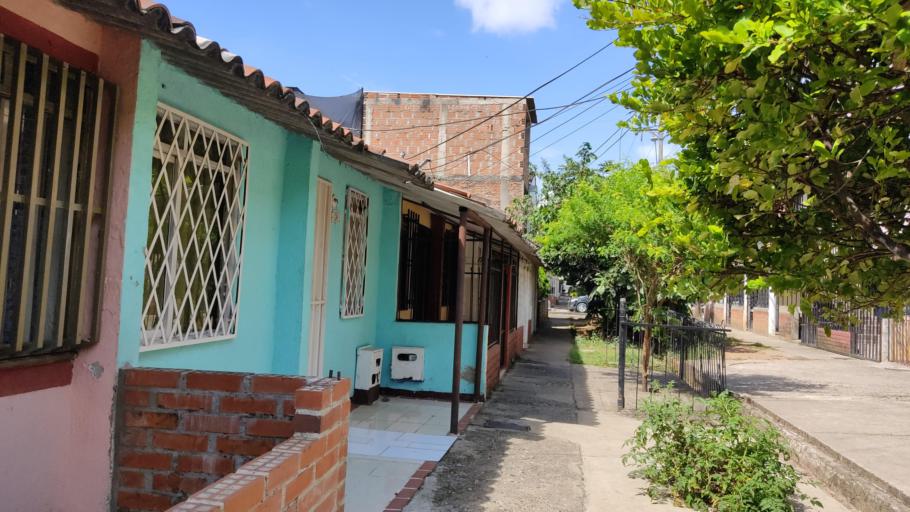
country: CO
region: Valle del Cauca
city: Jamundi
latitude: 3.2558
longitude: -76.5445
